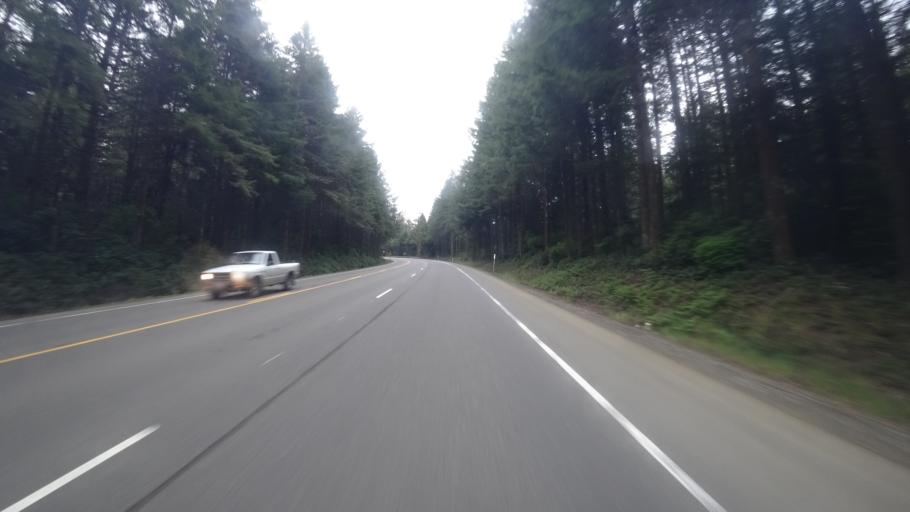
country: US
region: Oregon
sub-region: Coos County
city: Coquille
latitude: 43.2184
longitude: -124.3062
